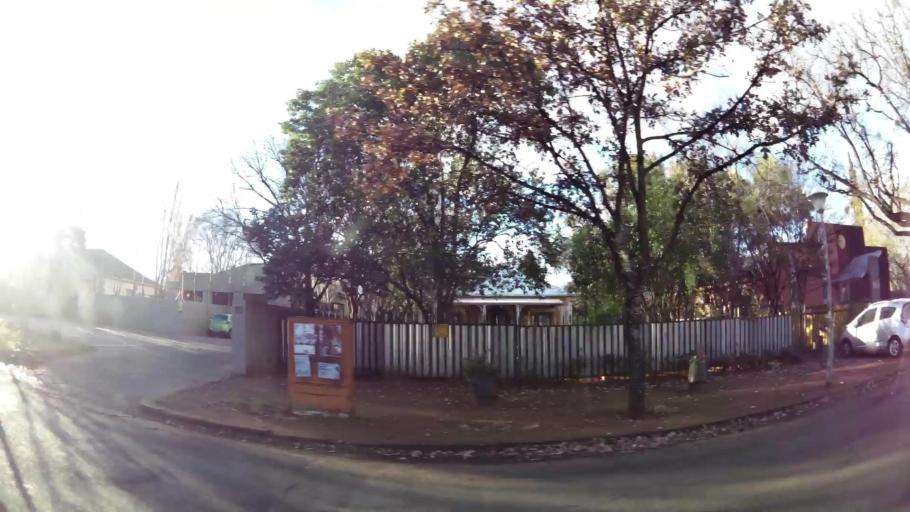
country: ZA
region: North-West
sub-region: Dr Kenneth Kaunda District Municipality
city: Potchefstroom
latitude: -26.7070
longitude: 27.0924
